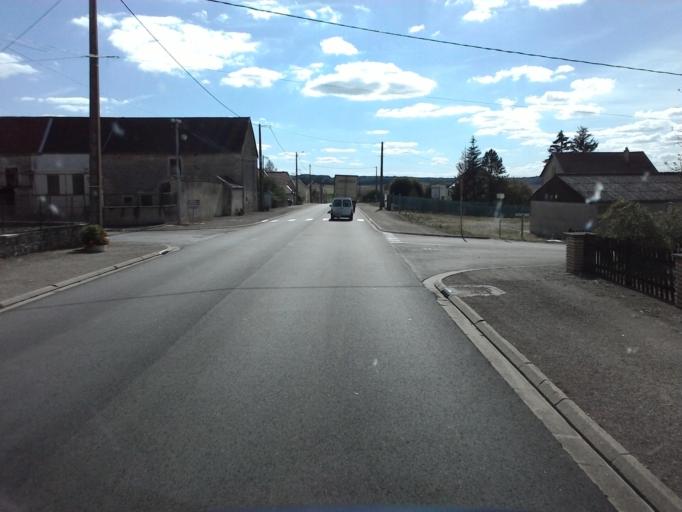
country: FR
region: Bourgogne
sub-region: Departement de la Cote-d'Or
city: Chatillon-sur-Seine
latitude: 47.8098
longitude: 4.5293
